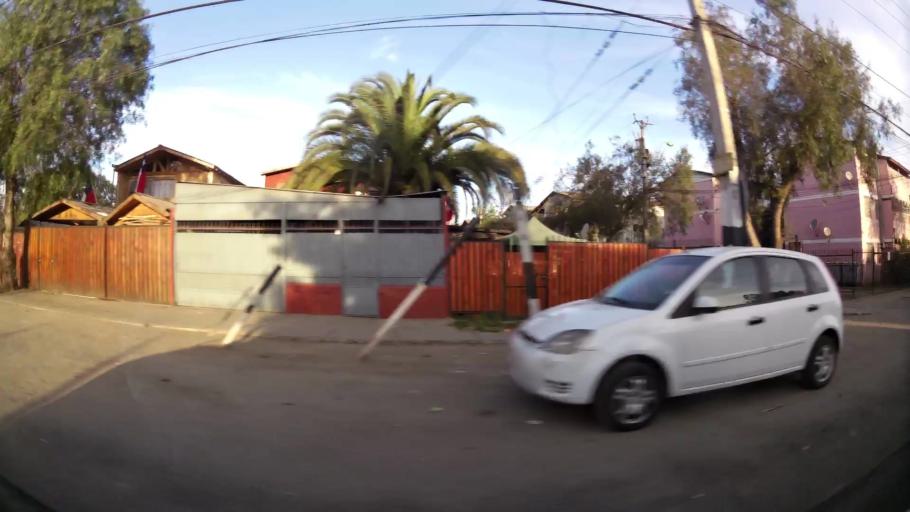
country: CL
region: Santiago Metropolitan
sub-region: Provincia de Santiago
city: Lo Prado
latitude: -33.4378
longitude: -70.7219
